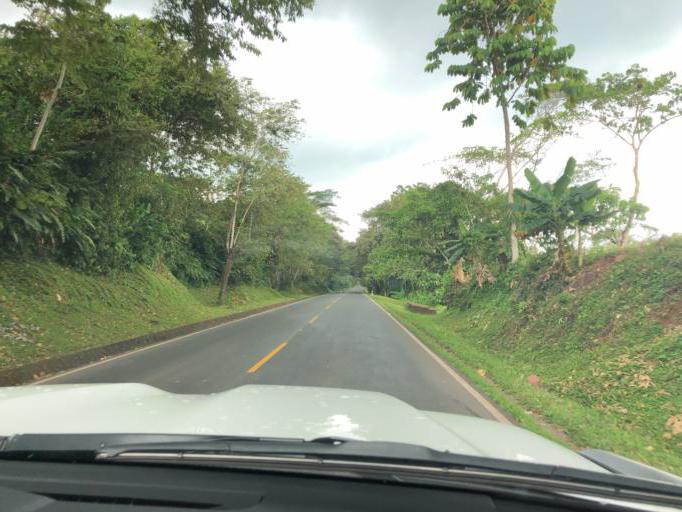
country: NI
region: Chontales
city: Villa Sandino
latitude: 11.9904
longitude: -84.8185
